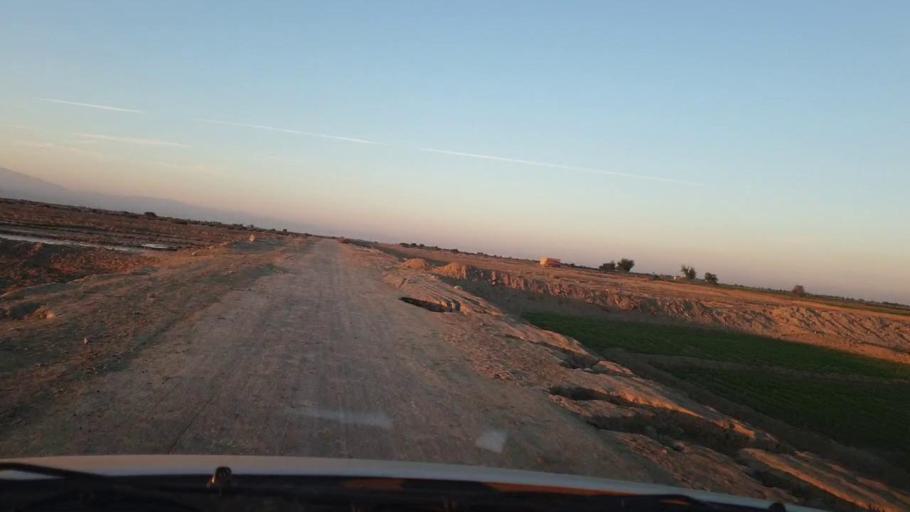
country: PK
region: Sindh
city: Johi
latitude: 26.8389
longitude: 67.4412
